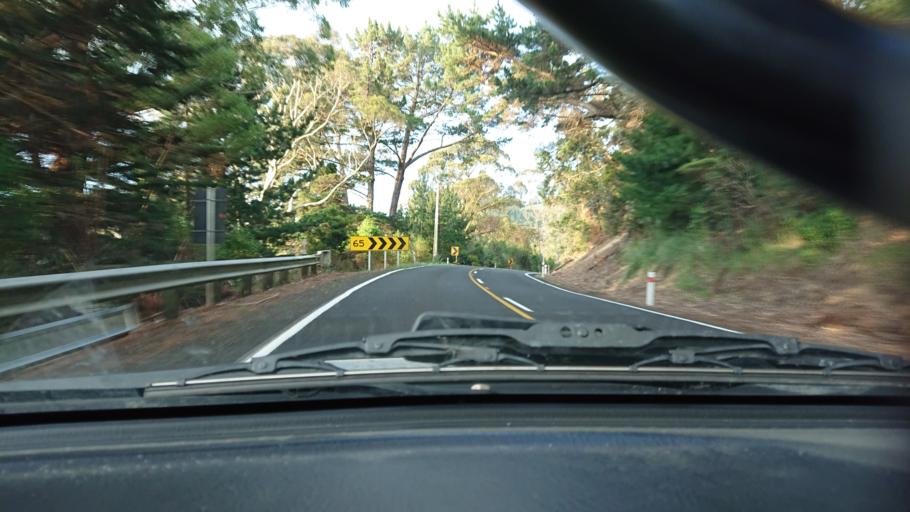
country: NZ
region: Auckland
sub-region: Auckland
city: Parakai
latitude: -36.5377
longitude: 174.4559
